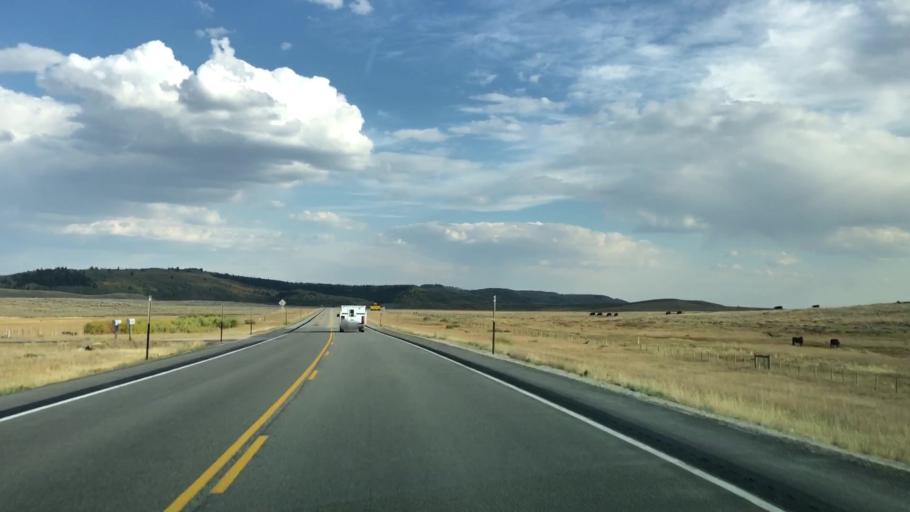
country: US
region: Wyoming
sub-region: Sublette County
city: Pinedale
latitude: 43.1258
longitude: -110.1888
